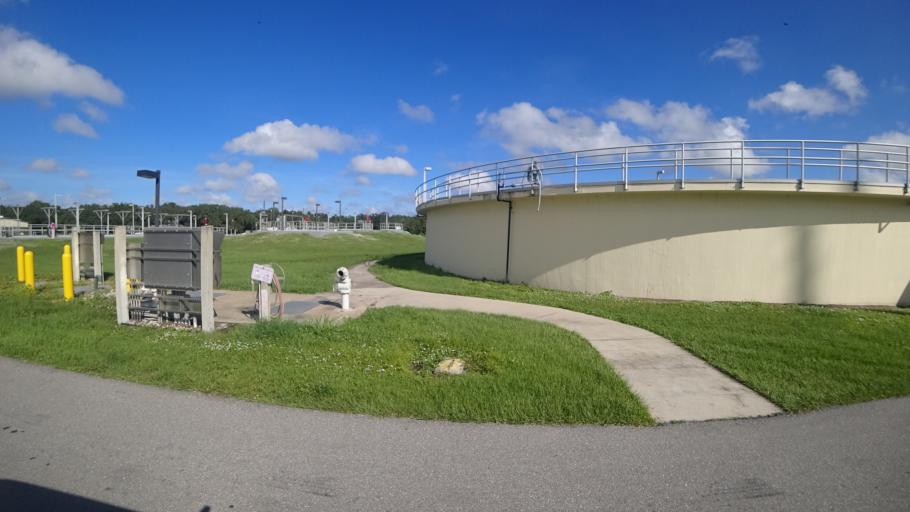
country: US
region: Florida
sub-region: Manatee County
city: Ellenton
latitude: 27.5841
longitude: -82.4774
